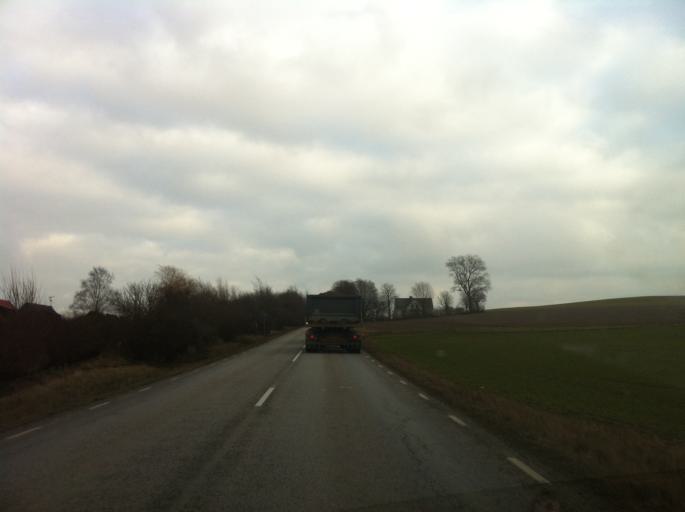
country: SE
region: Skane
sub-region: Kavlinge Kommun
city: Loddekopinge
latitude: 55.8188
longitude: 13.0322
